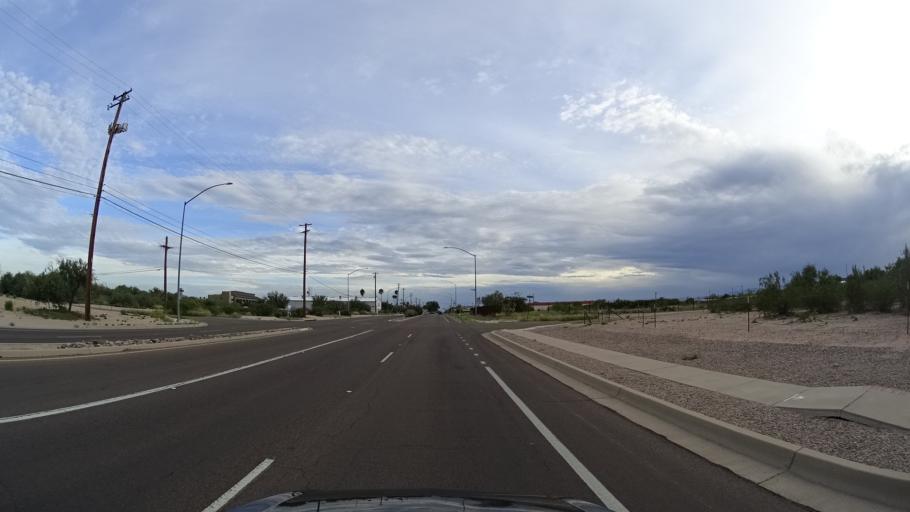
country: US
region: Arizona
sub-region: Pima County
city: South Tucson
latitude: 32.1383
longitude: -110.9348
